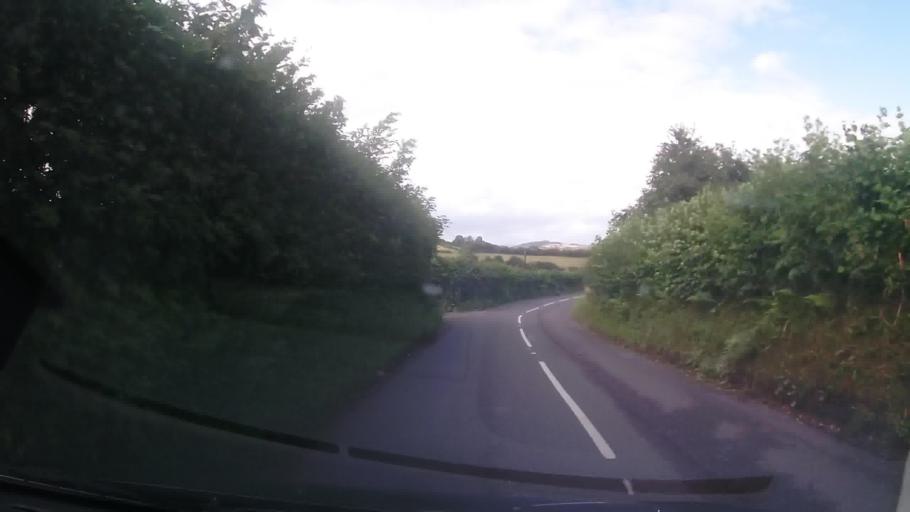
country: GB
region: England
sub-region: Shropshire
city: Acton
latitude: 52.4114
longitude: -3.0424
